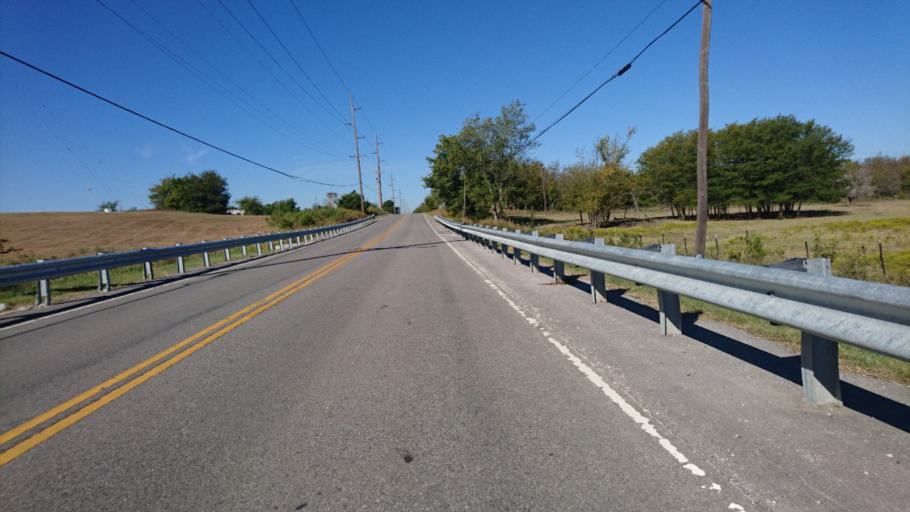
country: US
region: Oklahoma
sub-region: Rogers County
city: Catoosa
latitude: 36.1480
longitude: -95.8053
